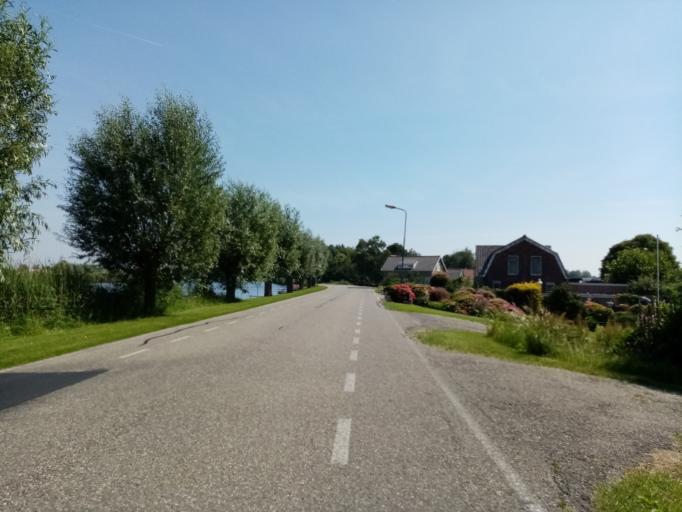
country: NL
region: North Holland
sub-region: Gemeente Aalsmeer
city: Aalsmeer
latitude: 52.2224
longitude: 4.7714
